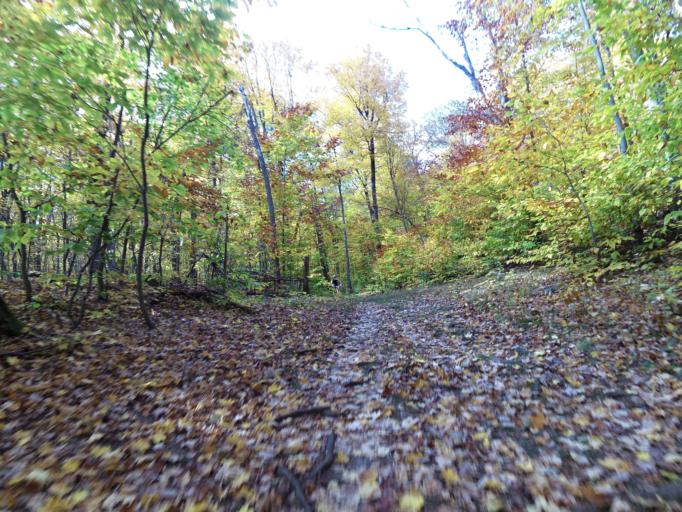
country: CA
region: Quebec
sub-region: Outaouais
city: Gatineau
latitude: 45.4785
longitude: -75.8382
